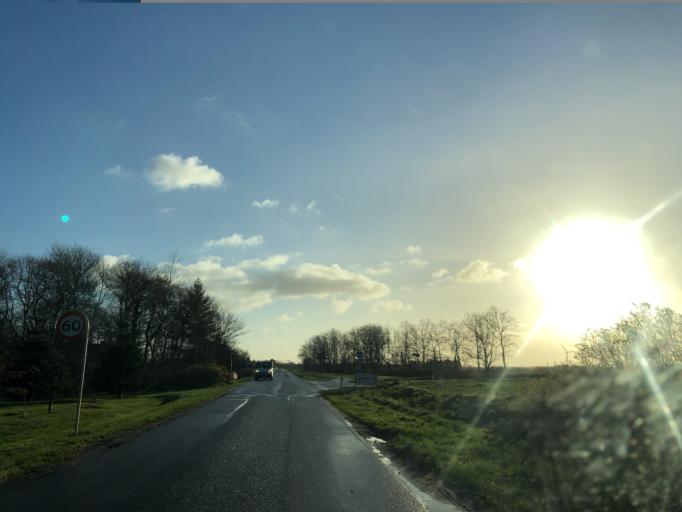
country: DK
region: Central Jutland
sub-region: Holstebro Kommune
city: Ulfborg
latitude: 56.2050
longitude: 8.2581
